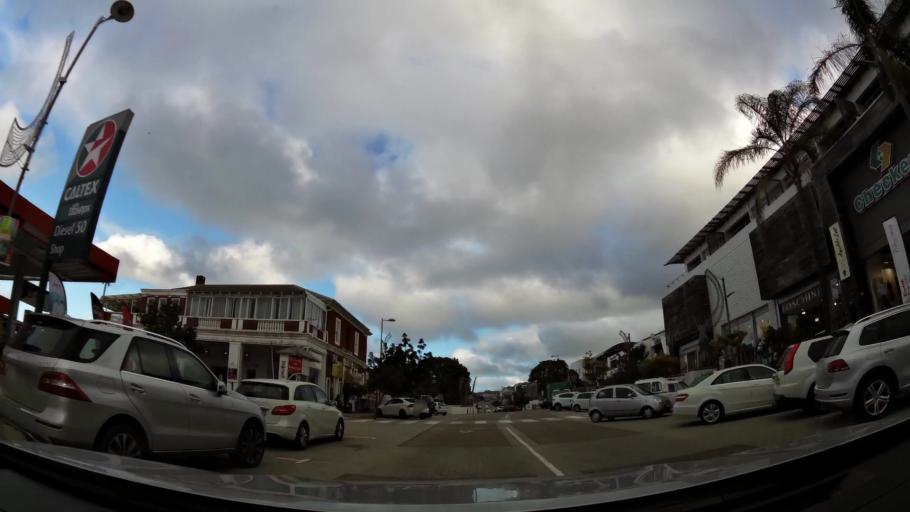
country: ZA
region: Western Cape
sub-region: Eden District Municipality
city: Plettenberg Bay
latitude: -34.0542
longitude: 23.3724
